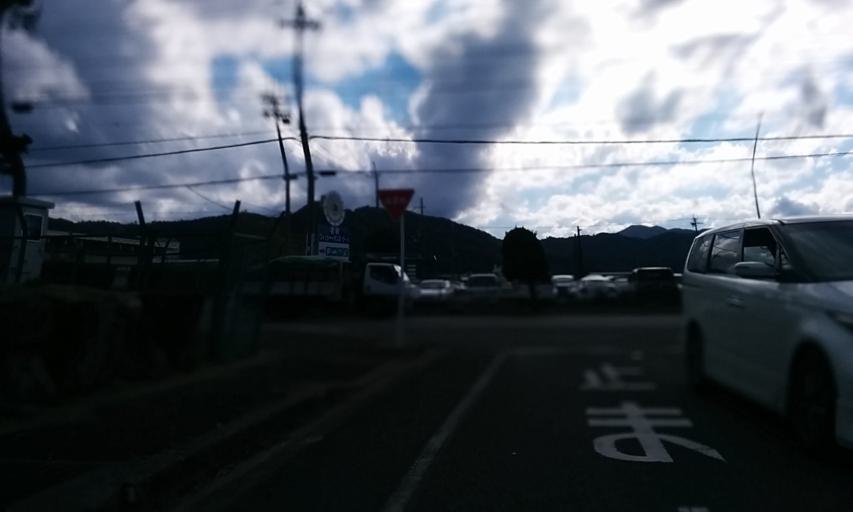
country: JP
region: Fukui
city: Obama
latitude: 35.5007
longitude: 135.7413
